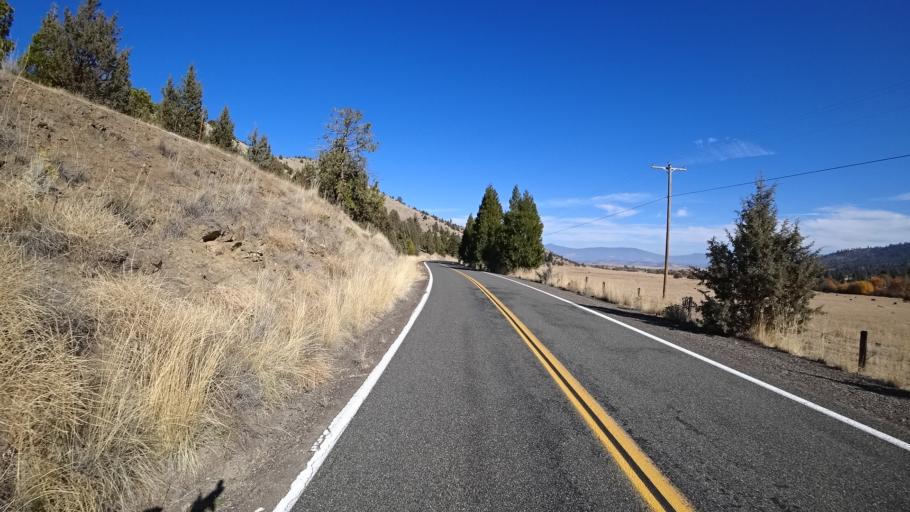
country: US
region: California
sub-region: Siskiyou County
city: Weed
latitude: 41.4848
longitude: -122.5705
